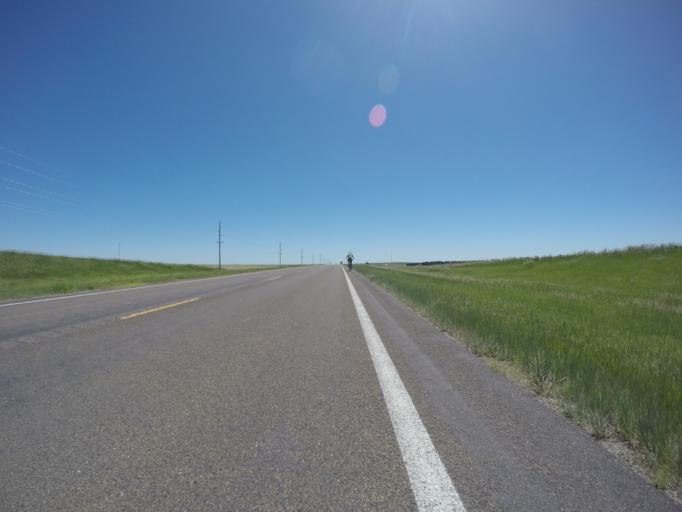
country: US
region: Kansas
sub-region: Norton County
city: Norton
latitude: 39.8284
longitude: -99.6196
